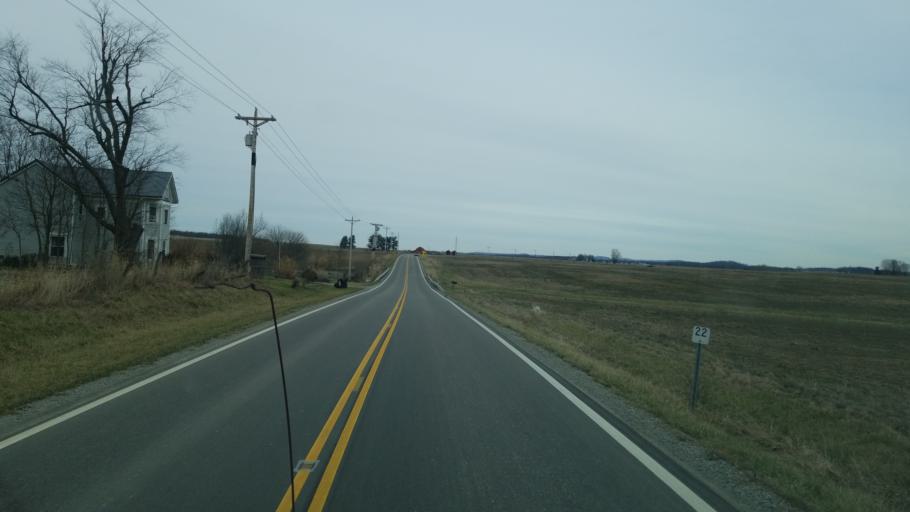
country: US
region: Ohio
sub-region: Highland County
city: Leesburg
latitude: 39.2616
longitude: -83.5341
